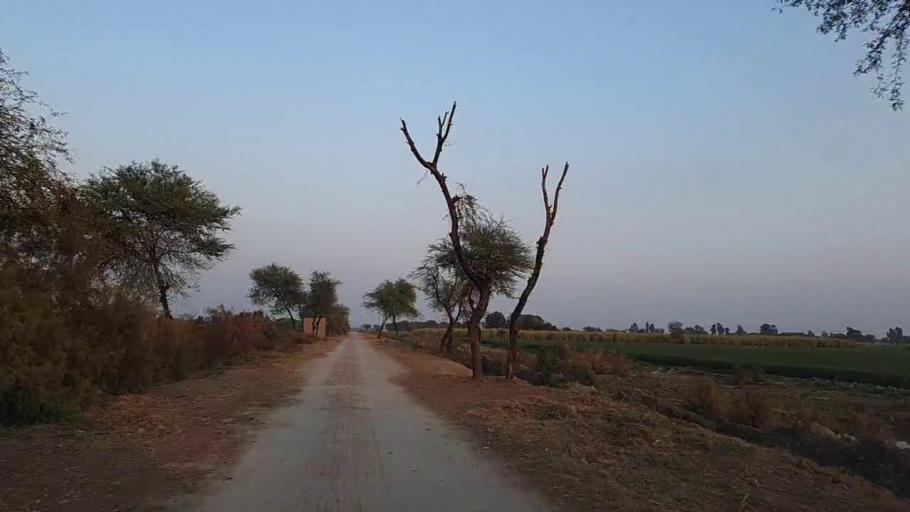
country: PK
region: Sindh
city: Jam Sahib
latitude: 26.3091
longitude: 68.5799
